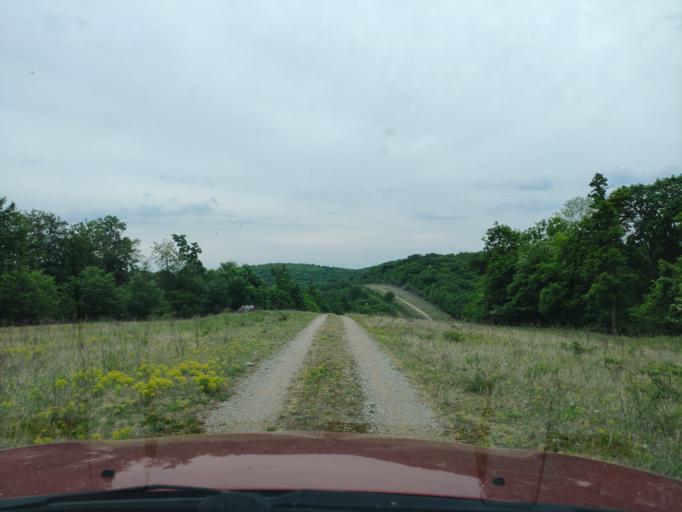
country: SK
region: Kosicky
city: Roznava
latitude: 48.5457
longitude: 20.5853
